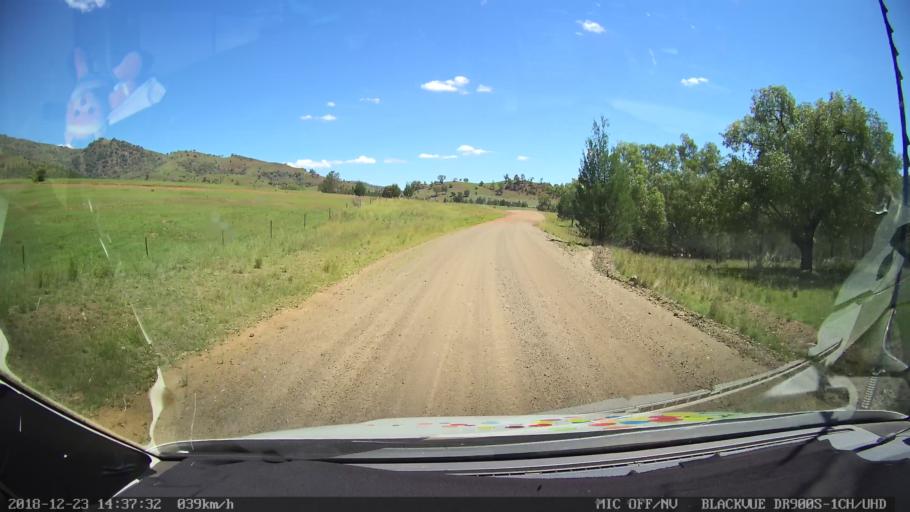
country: AU
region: New South Wales
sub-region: Tamworth Municipality
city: Manilla
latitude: -30.6161
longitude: 150.9071
